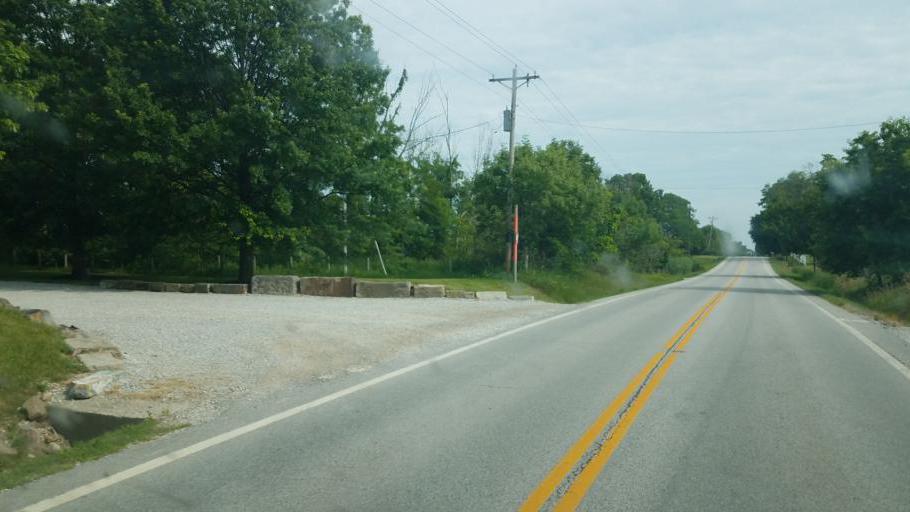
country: US
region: Ohio
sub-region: Medina County
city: Lodi
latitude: 41.1134
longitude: -82.0243
